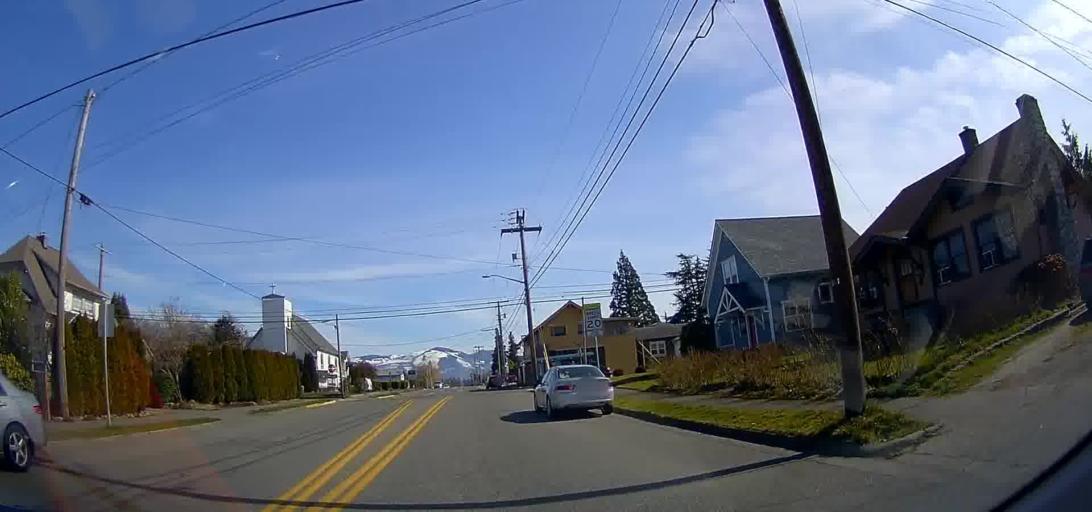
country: US
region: Washington
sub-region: Skagit County
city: Mount Vernon
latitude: 48.4211
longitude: -122.3295
